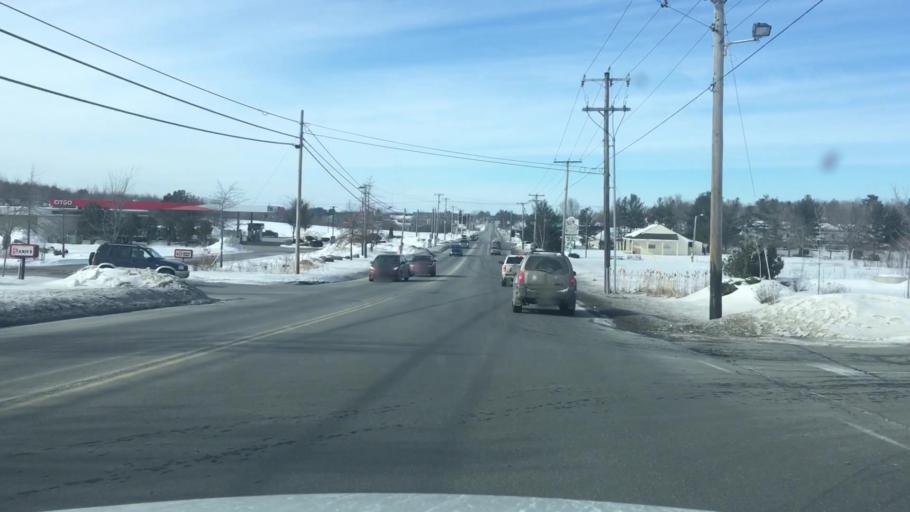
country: US
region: Maine
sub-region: Penobscot County
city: Bangor
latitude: 44.8345
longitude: -68.7898
